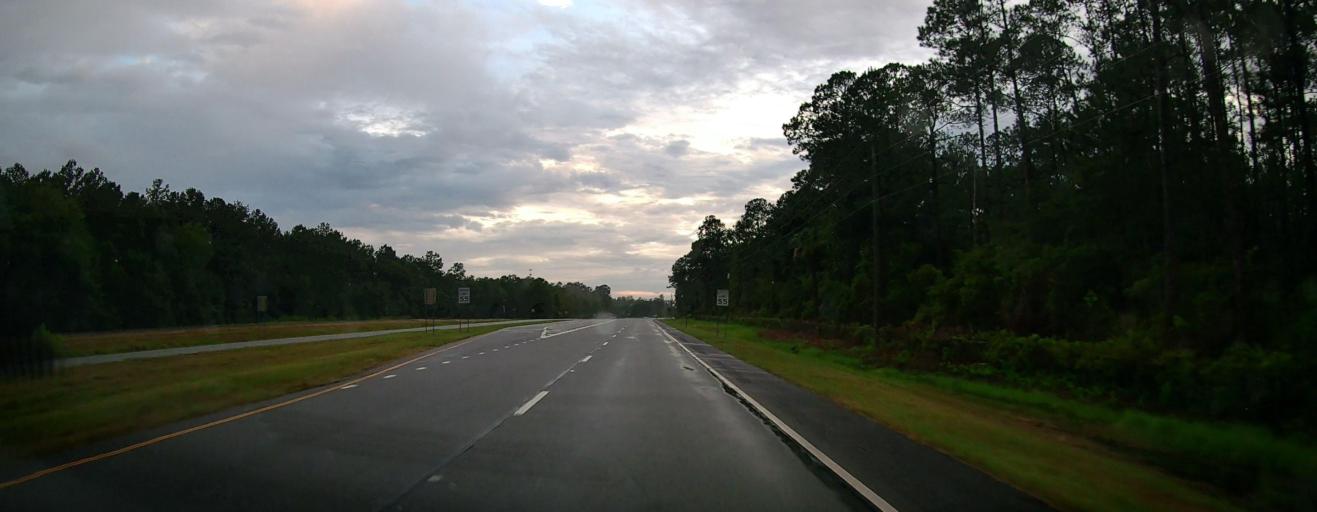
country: US
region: Georgia
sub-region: Lanier County
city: Lakeland
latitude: 30.9436
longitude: -82.9879
